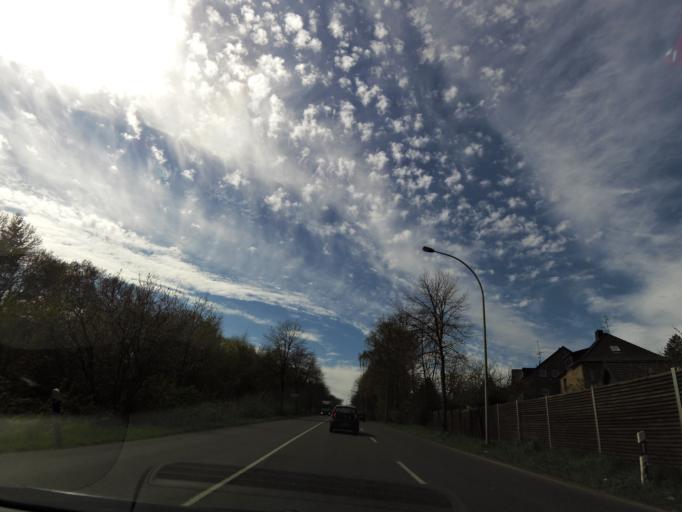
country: DE
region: North Rhine-Westphalia
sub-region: Regierungsbezirk Koln
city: Herzogenrath
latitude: 50.8644
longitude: 6.0862
